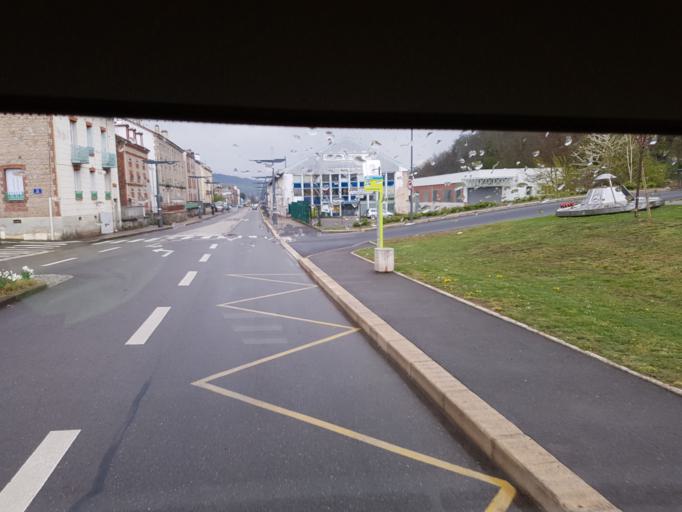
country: FR
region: Rhone-Alpes
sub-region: Departement de la Loire
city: Le Chambon-Feugerolles
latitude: 45.3958
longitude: 4.3183
